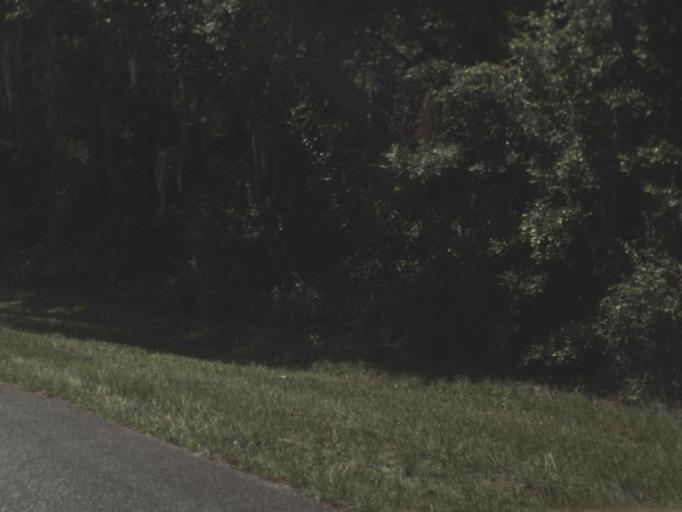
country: US
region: Florida
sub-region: Putnam County
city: Crescent City
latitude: 29.4690
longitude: -81.5293
